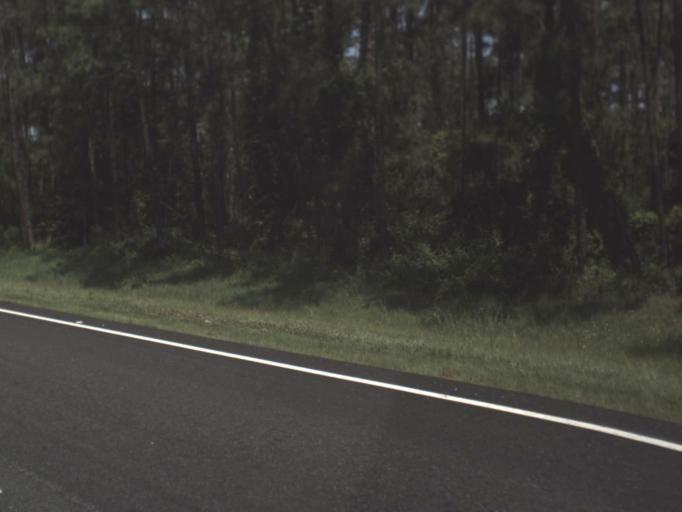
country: US
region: Florida
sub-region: Duval County
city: Baldwin
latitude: 30.2886
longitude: -81.9904
